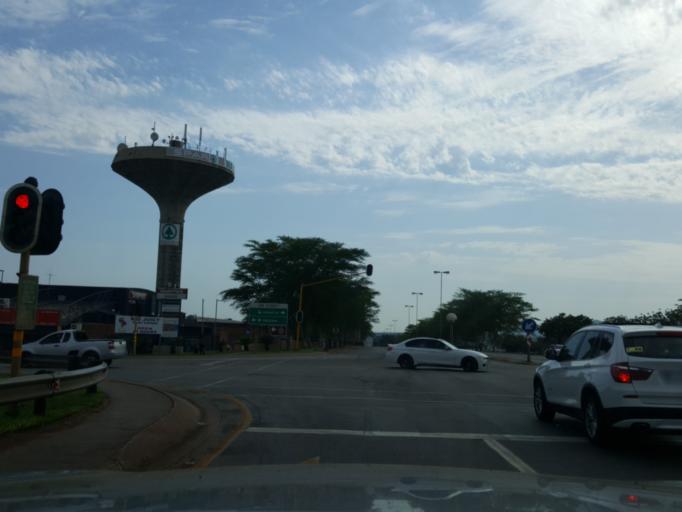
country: SZ
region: Hhohho
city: Ntfonjeni
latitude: -25.4996
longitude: 31.5086
